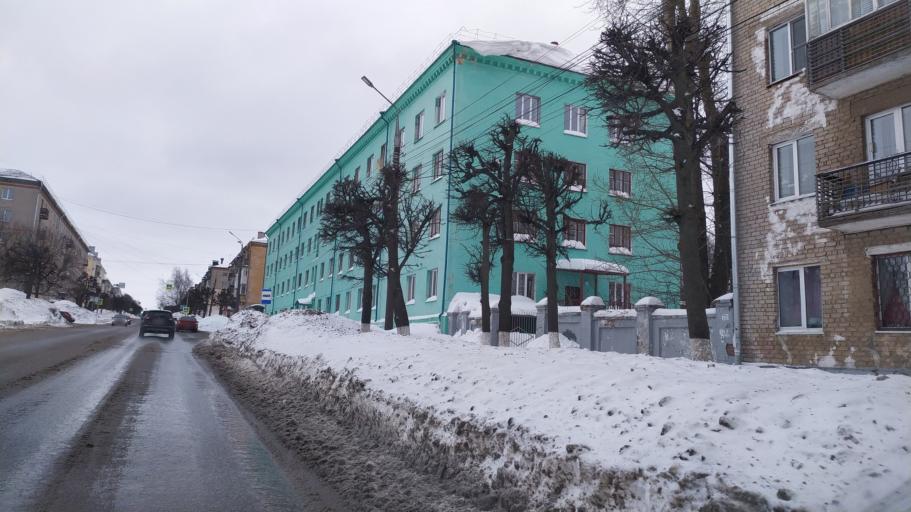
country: RU
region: Chuvashia
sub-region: Cheboksarskiy Rayon
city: Cheboksary
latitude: 56.1225
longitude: 47.2579
